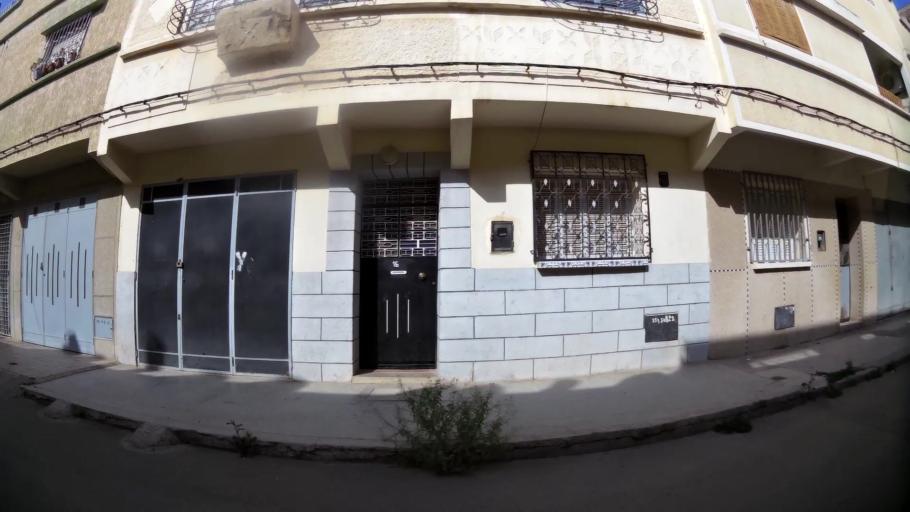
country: MA
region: Oriental
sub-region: Oujda-Angad
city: Oujda
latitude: 34.6885
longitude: -1.9036
